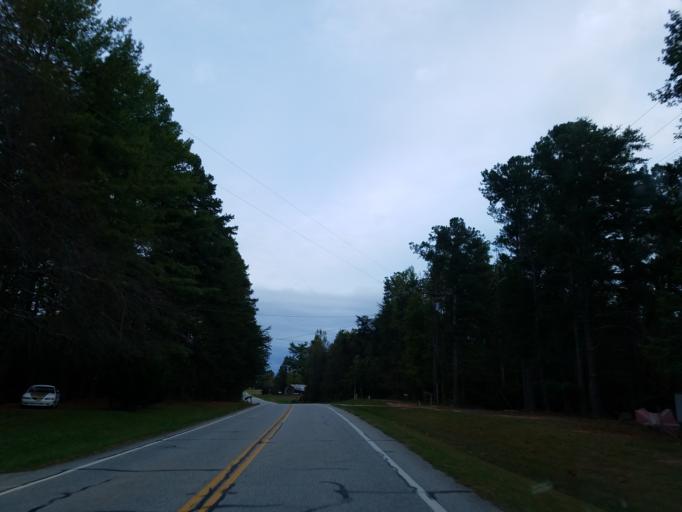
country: US
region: Georgia
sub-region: Dawson County
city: Dawsonville
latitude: 34.4470
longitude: -84.1673
